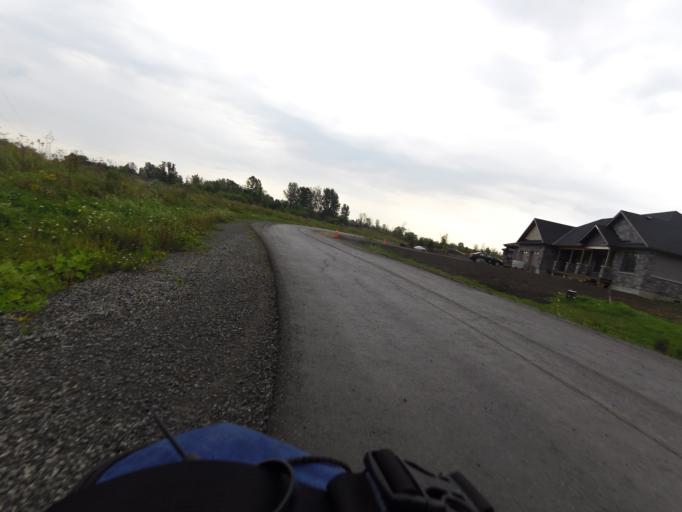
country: CA
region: Ontario
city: Ottawa
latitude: 45.2286
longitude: -75.4745
